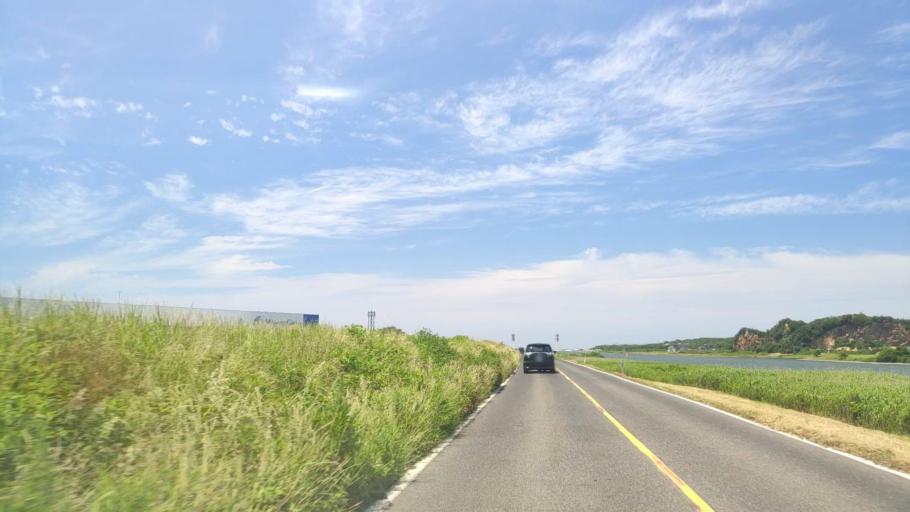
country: JP
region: Tottori
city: Tottori
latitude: 35.5231
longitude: 134.2062
